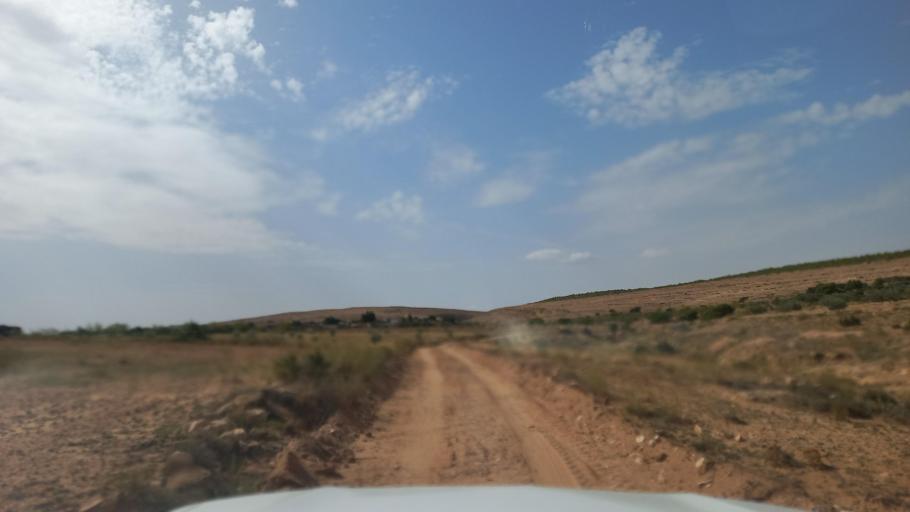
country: TN
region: Al Qasrayn
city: Kasserine
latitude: 35.3637
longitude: 8.8589
